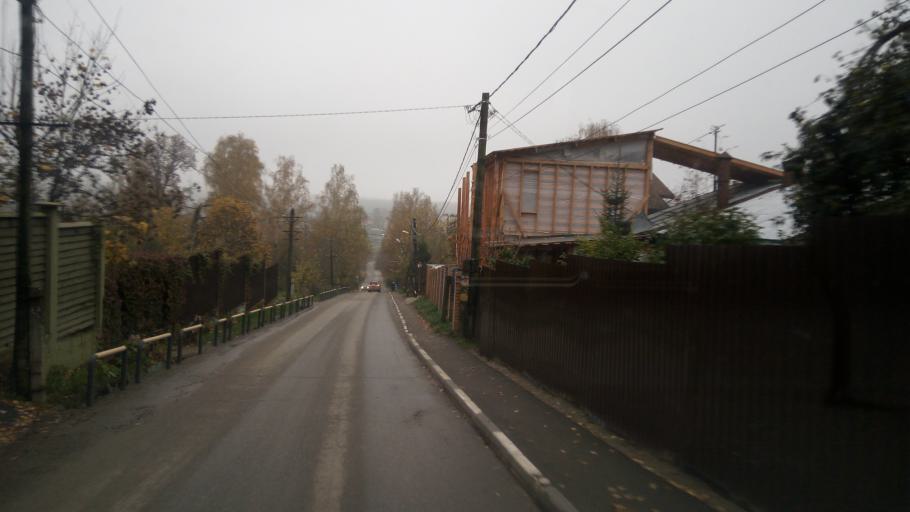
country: RU
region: Moskovskaya
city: Skhodnya
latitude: 55.9397
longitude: 37.2896
